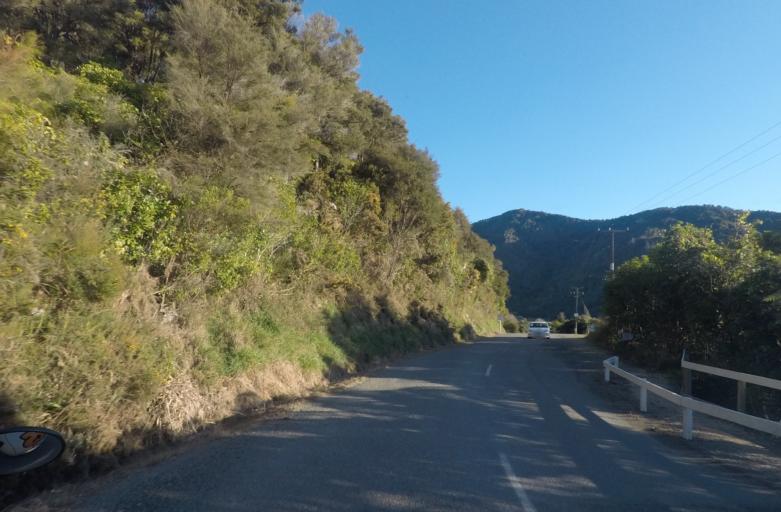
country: NZ
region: Marlborough
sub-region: Marlborough District
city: Picton
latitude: -41.2738
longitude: 173.9679
